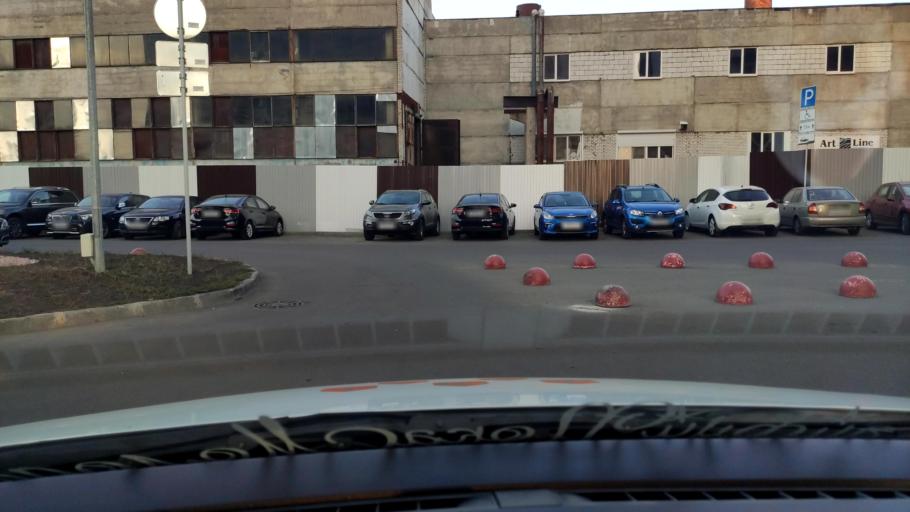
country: RU
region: Voronezj
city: Voronezh
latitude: 51.6684
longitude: 39.1769
